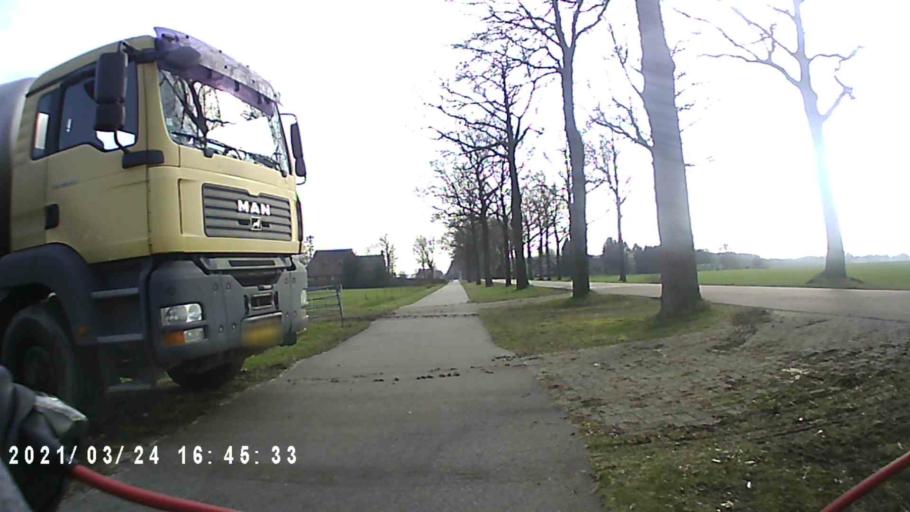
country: NL
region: Groningen
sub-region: Gemeente Leek
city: Leek
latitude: 53.0511
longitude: 6.2796
